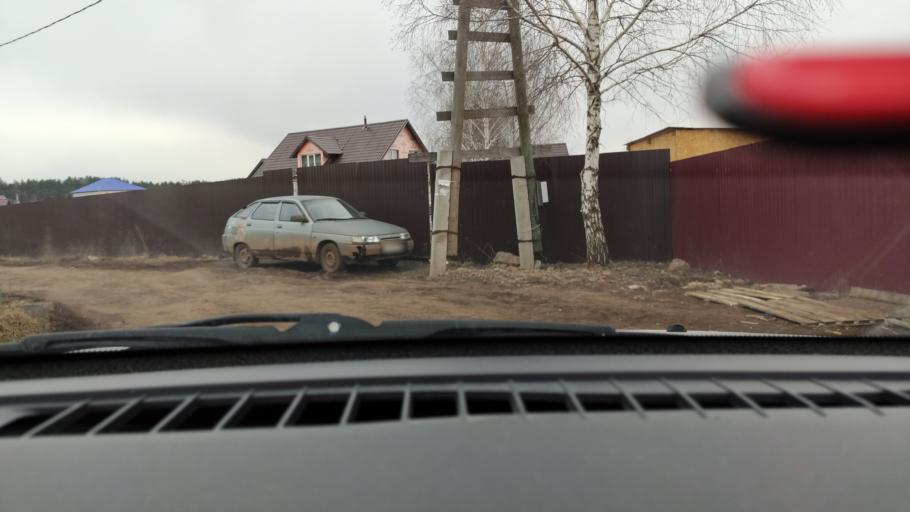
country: RU
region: Perm
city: Kultayevo
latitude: 57.8960
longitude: 56.0148
